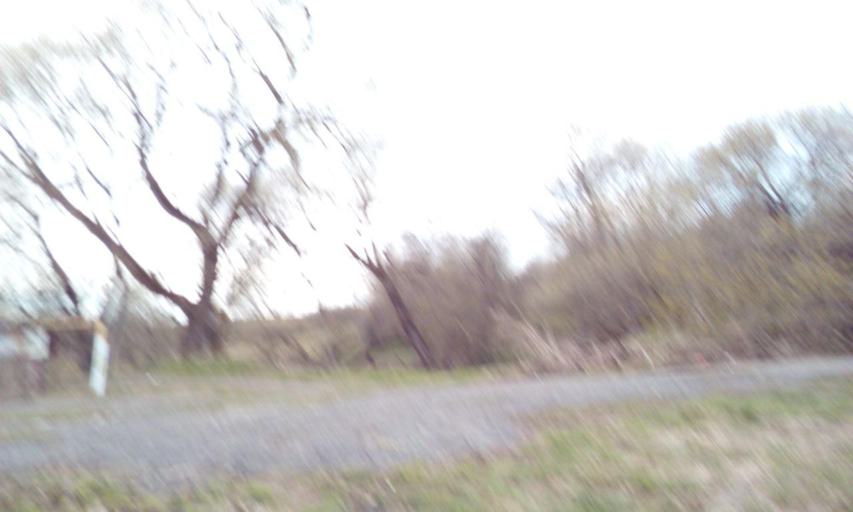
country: RU
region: Moskovskaya
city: Troitsk
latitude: 55.5162
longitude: 37.2635
